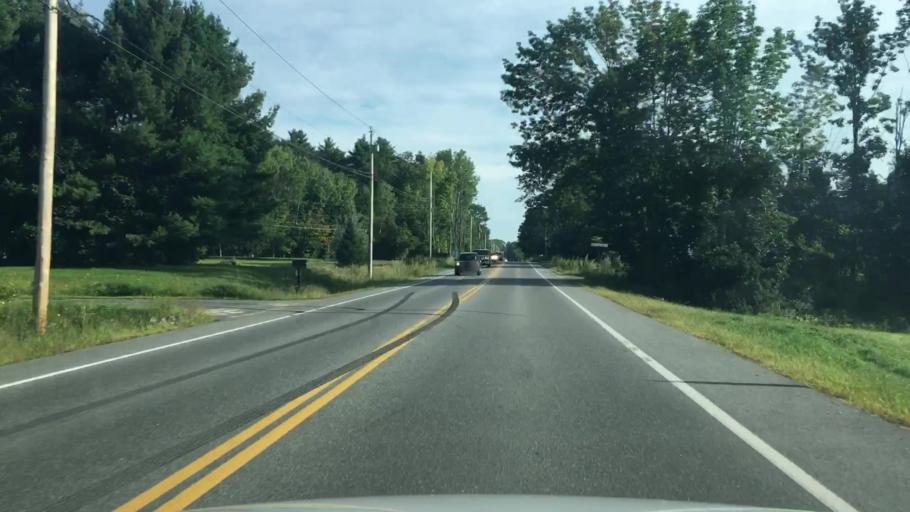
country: US
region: Maine
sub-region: Cumberland County
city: North Windham
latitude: 43.7846
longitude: -70.4397
